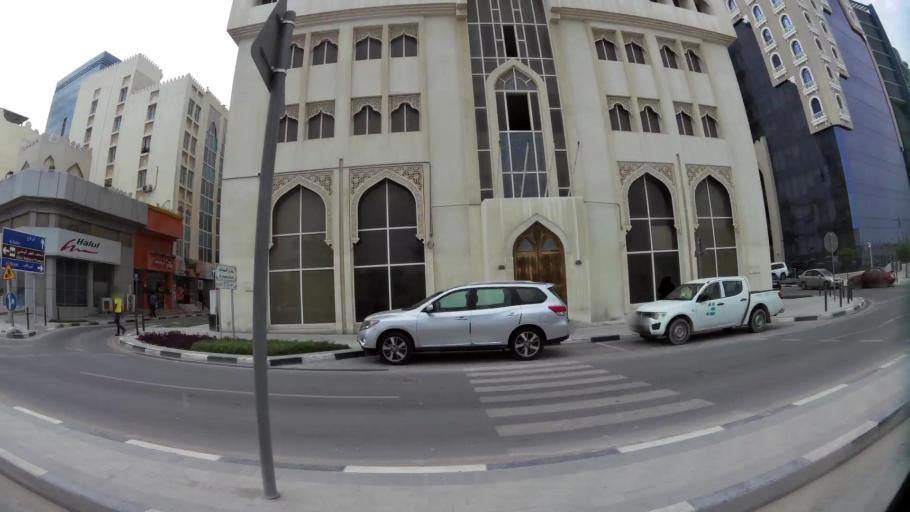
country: QA
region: Baladiyat ad Dawhah
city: Doha
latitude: 25.2877
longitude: 51.5477
